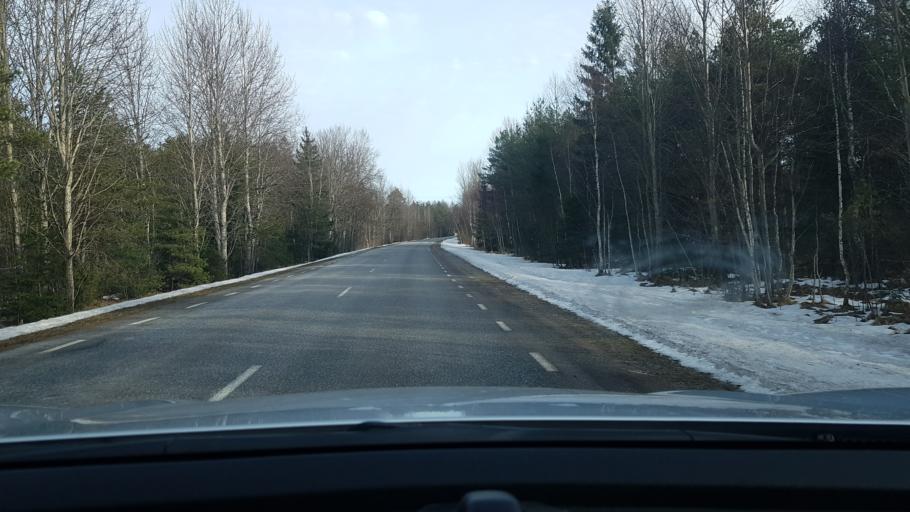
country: EE
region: Saare
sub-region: Kuressaare linn
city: Kuressaare
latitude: 58.4217
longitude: 22.6669
